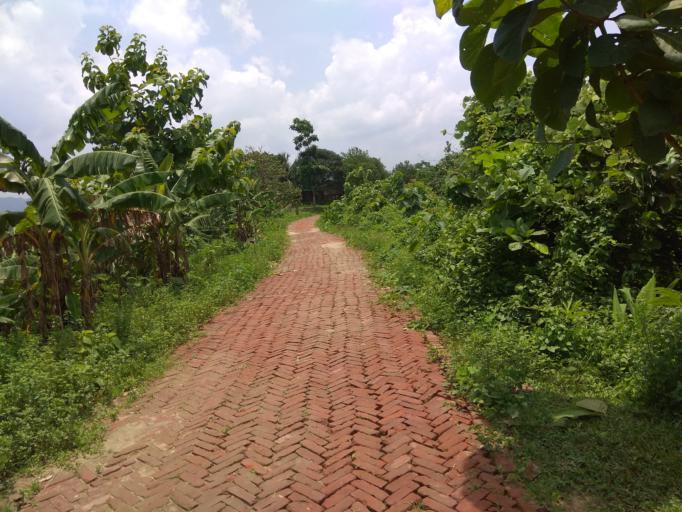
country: BD
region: Chittagong
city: Manikchari
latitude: 22.8854
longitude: 91.9252
